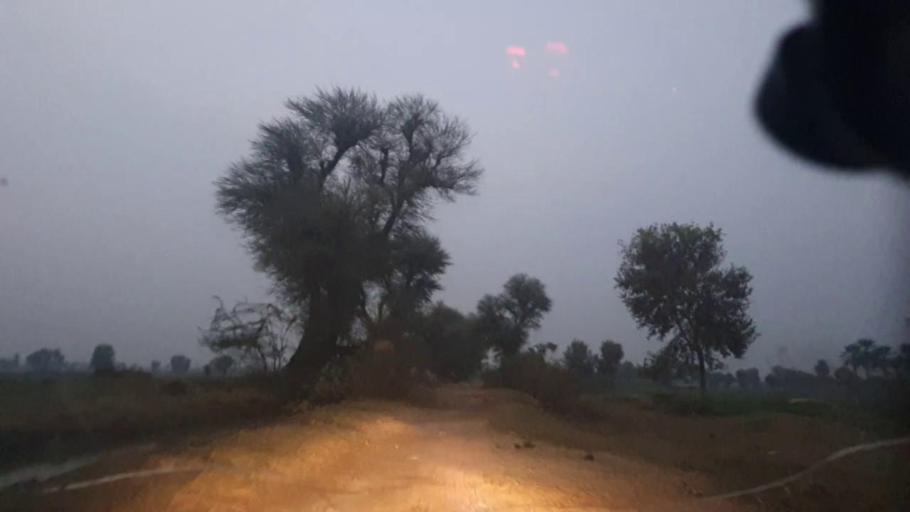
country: PK
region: Sindh
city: Hingorja
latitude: 27.2027
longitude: 68.3716
